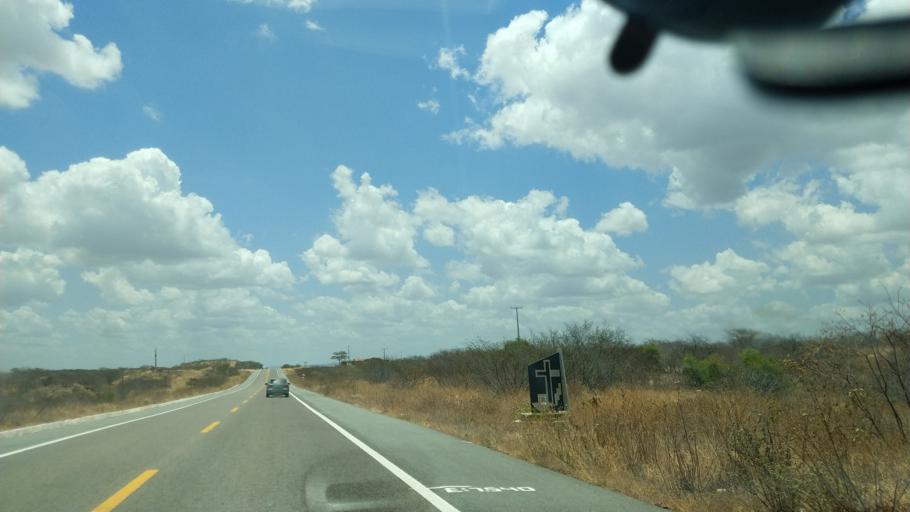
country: BR
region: Rio Grande do Norte
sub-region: Cerro Cora
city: Cerro Cora
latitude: -6.2074
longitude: -36.3166
